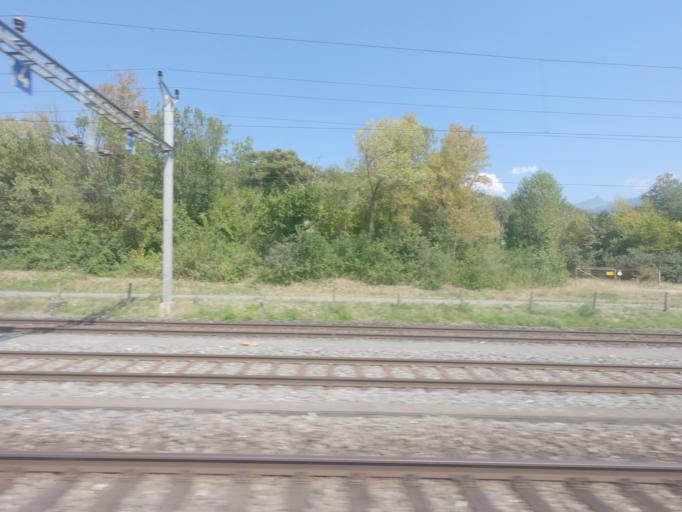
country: CH
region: Vaud
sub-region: Aigle District
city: Ollon
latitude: 46.2835
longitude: 6.9705
